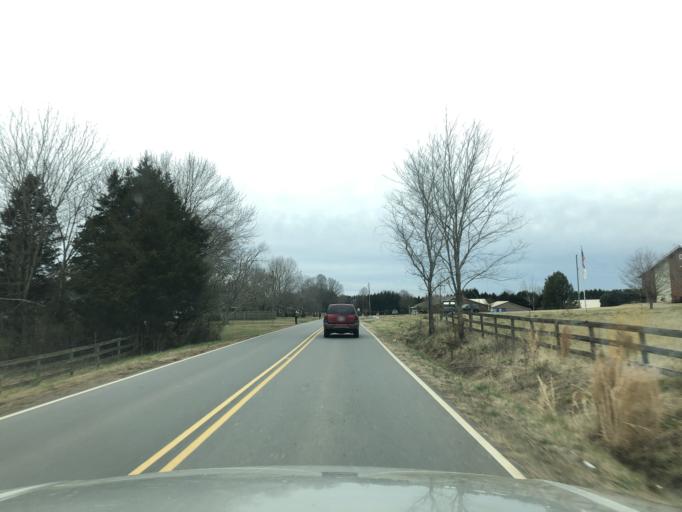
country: US
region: North Carolina
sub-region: Cleveland County
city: Shelby
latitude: 35.3429
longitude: -81.5102
